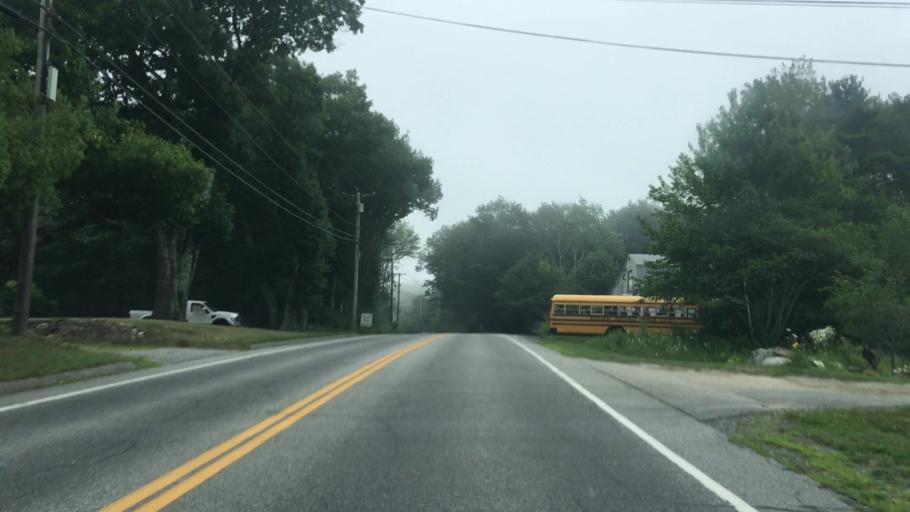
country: US
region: Maine
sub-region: Lincoln County
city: Boothbay
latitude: 43.9034
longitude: -69.6219
